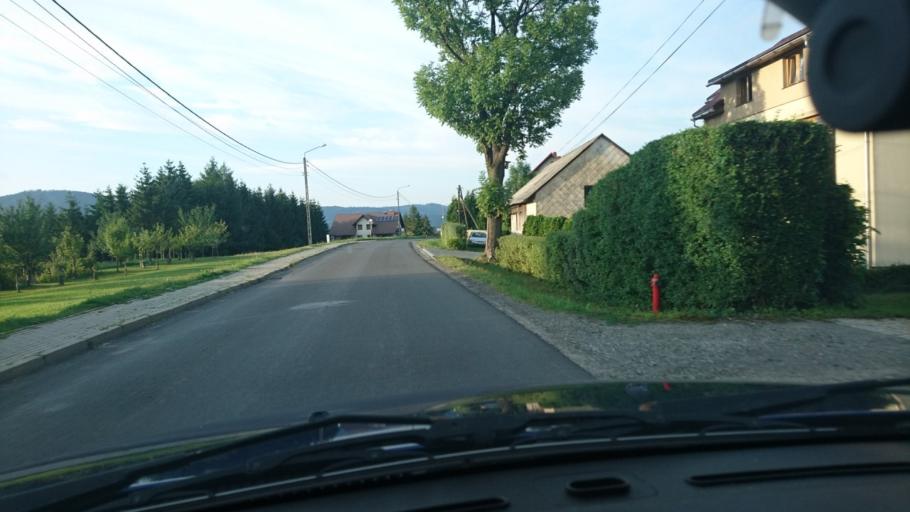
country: PL
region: Silesian Voivodeship
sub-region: Powiat cieszynski
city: Jaworzynka
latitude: 49.5455
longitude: 18.8787
